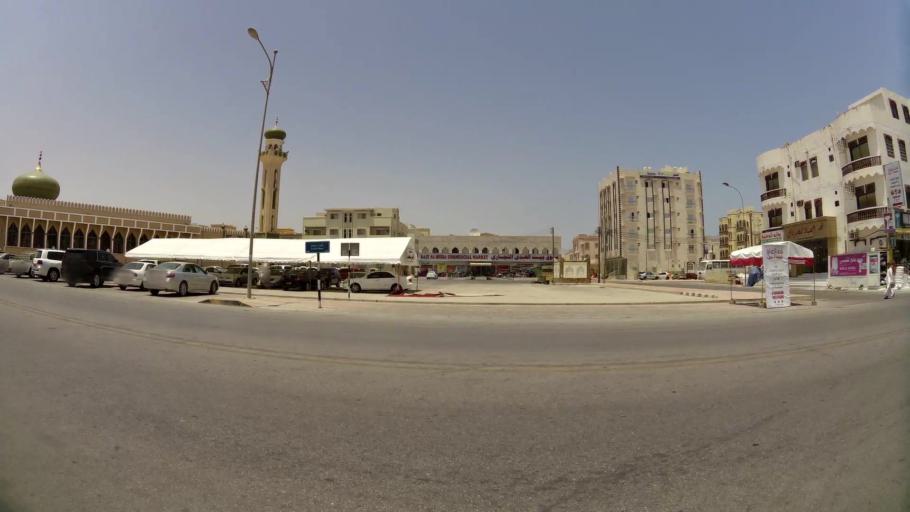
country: OM
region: Zufar
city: Salalah
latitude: 17.0191
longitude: 54.0845
